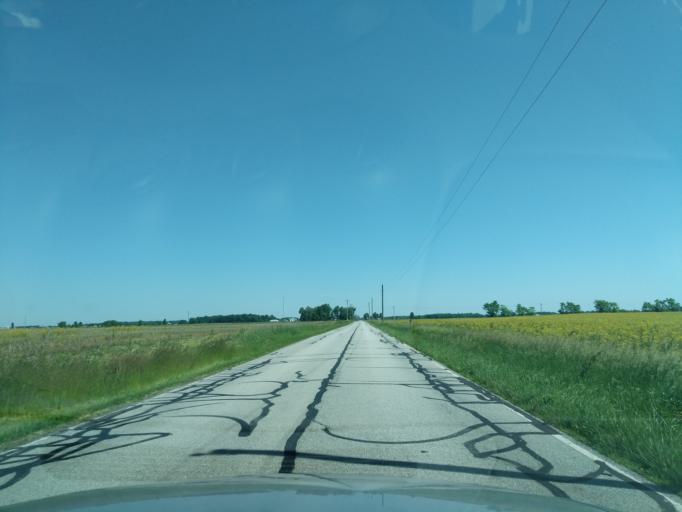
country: US
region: Indiana
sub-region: Huntington County
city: Warren
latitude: 40.6795
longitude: -85.5067
